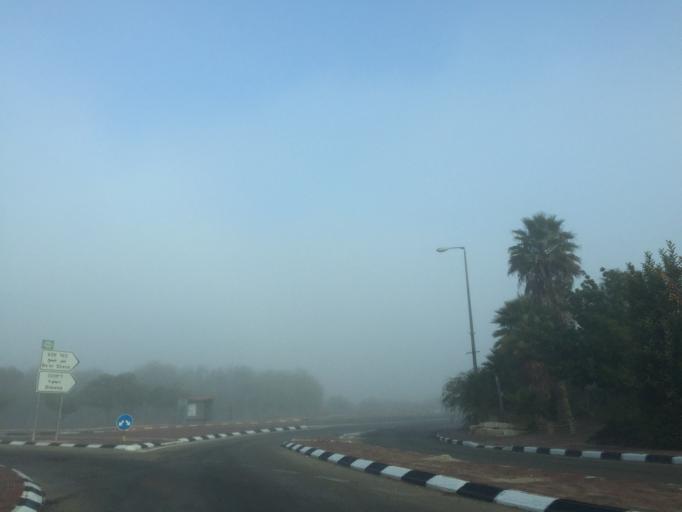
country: IL
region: Southern District
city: Yeroham
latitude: 30.9900
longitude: 34.9119
